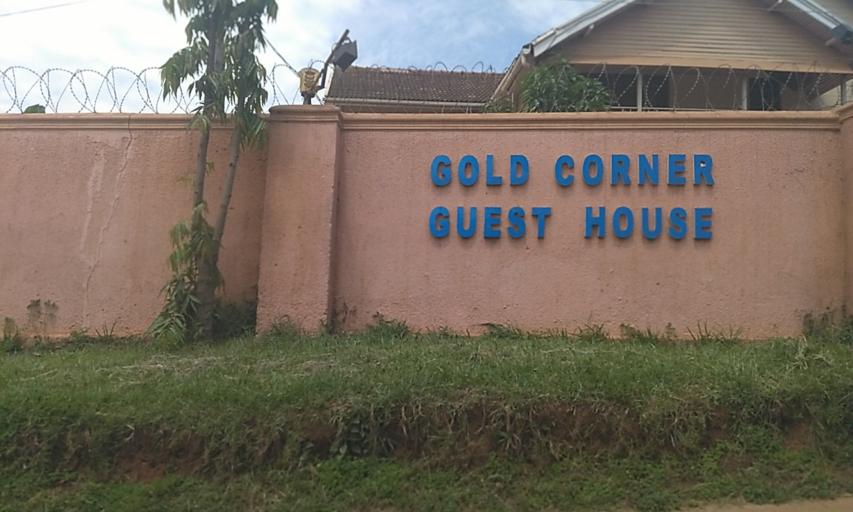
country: UG
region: Central Region
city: Kampala Central Division
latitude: 0.3060
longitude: 32.5612
